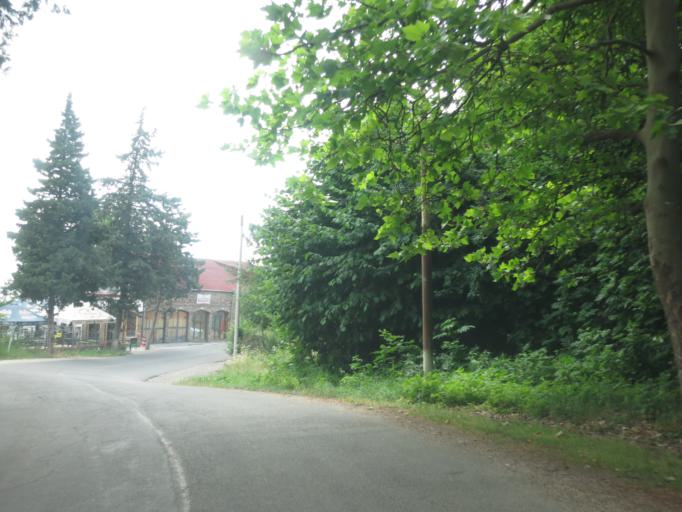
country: GE
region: Kakheti
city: Sighnaghi
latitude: 41.6135
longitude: 45.9227
